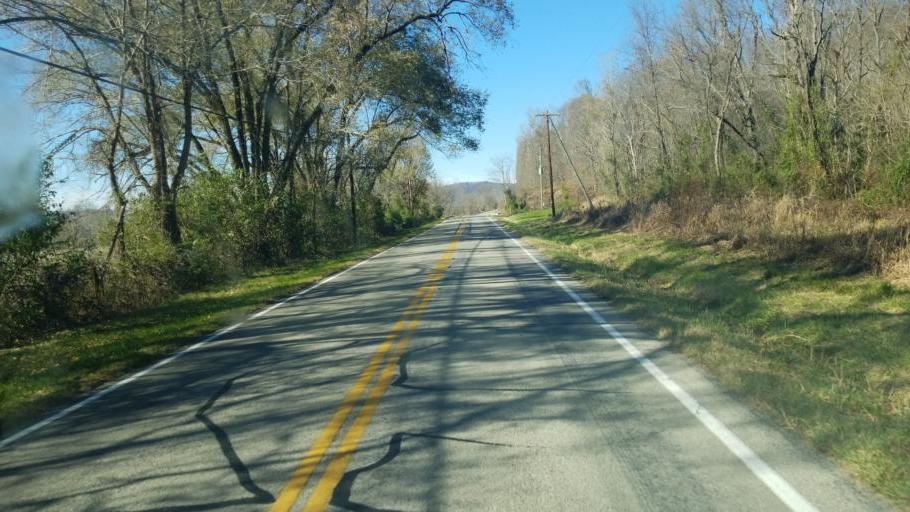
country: US
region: Kentucky
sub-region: Lewis County
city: Vanceburg
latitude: 38.6251
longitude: -83.1972
